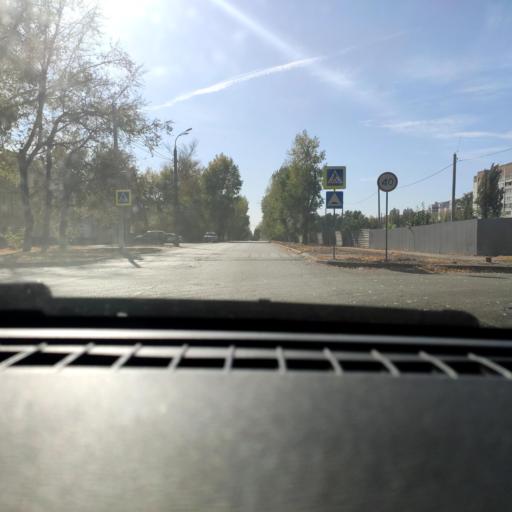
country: RU
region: Voronezj
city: Voronezh
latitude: 51.6674
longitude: 39.2539
